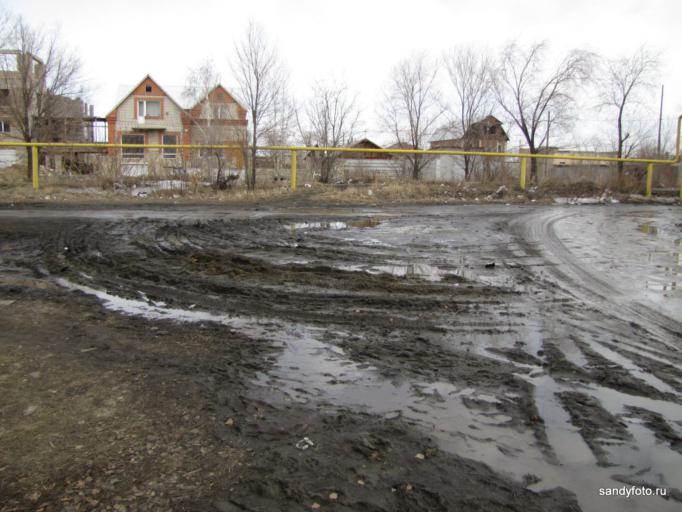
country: RU
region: Chelyabinsk
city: Troitsk
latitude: 54.1056
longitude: 61.5592
